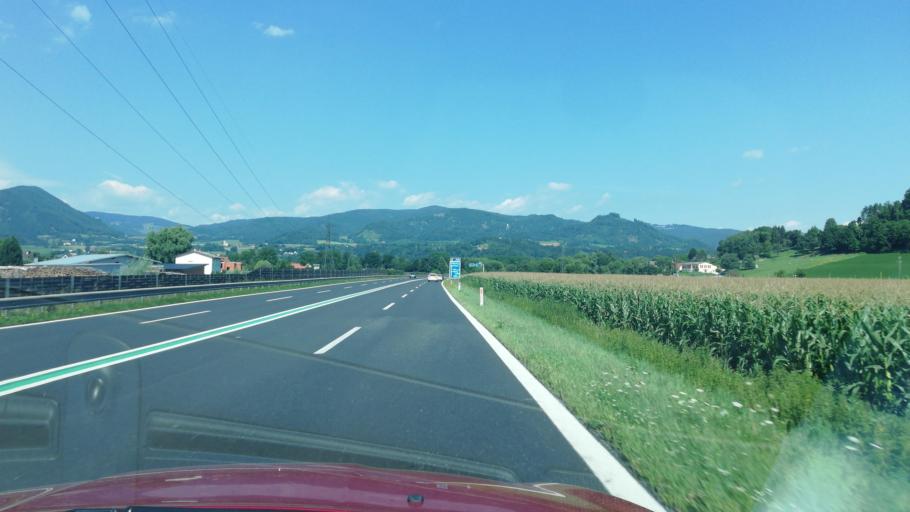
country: AT
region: Carinthia
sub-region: Politischer Bezirk Sankt Veit an der Glan
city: Sankt Veit an der Glan
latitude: 46.7599
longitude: 14.3857
